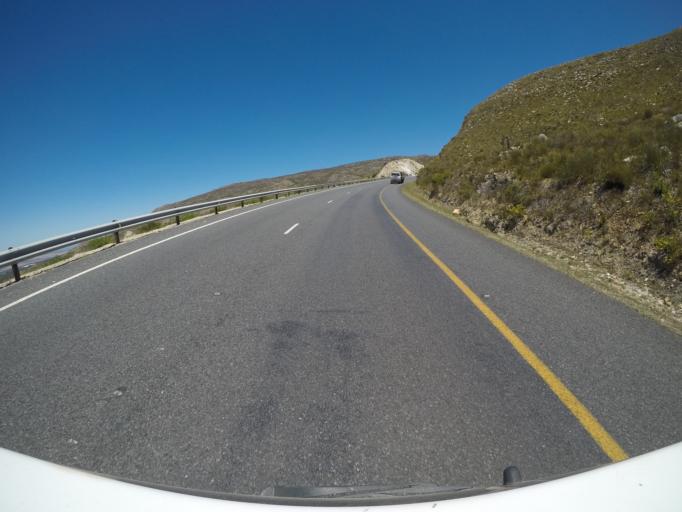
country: ZA
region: Western Cape
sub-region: Overberg District Municipality
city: Grabouw
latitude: -34.2217
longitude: 19.1823
